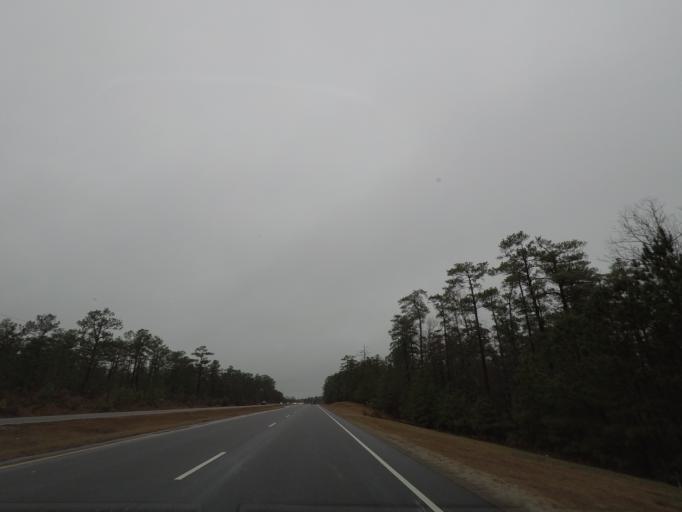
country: US
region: North Carolina
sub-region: Cumberland County
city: Spring Lake
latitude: 35.2387
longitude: -79.0208
